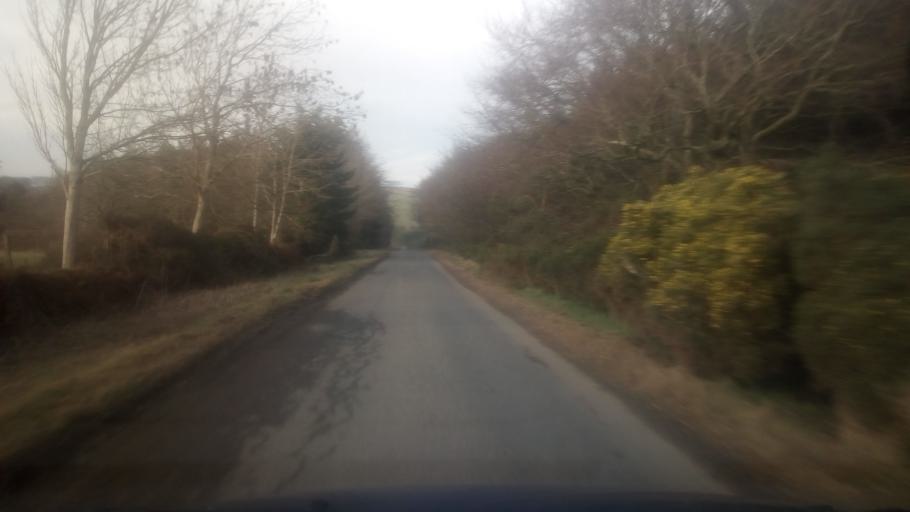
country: GB
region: Scotland
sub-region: The Scottish Borders
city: Jedburgh
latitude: 55.4044
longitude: -2.6010
